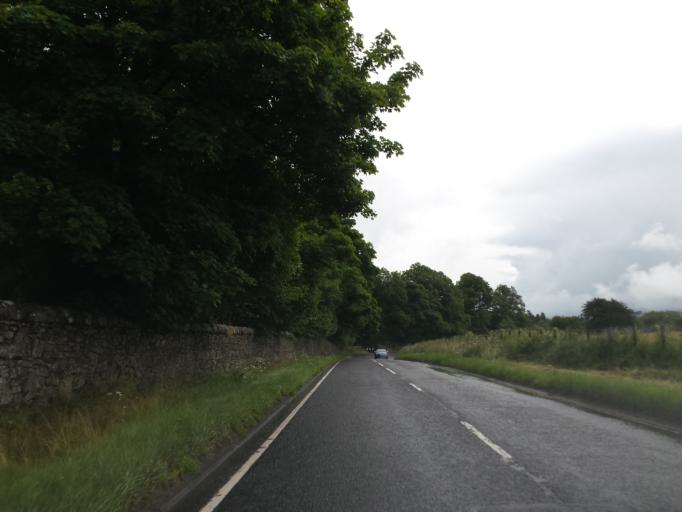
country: GB
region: Scotland
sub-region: Fife
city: Newburgh
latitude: 56.3469
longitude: -3.2687
